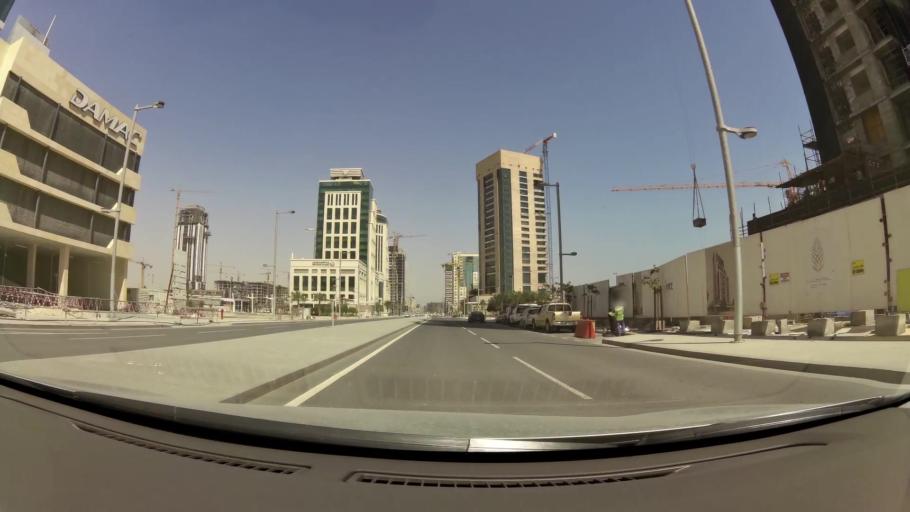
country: QA
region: Baladiyat ad Dawhah
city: Doha
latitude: 25.3911
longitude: 51.5231
